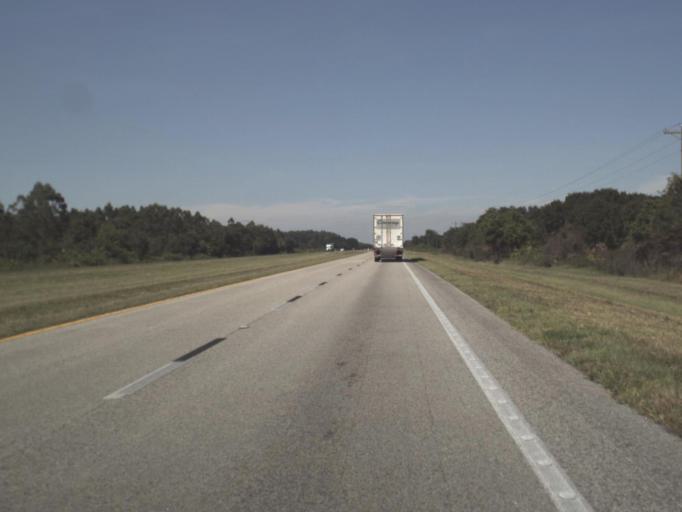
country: US
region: Florida
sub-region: Hendry County
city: Port LaBelle
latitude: 26.9837
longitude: -81.3223
